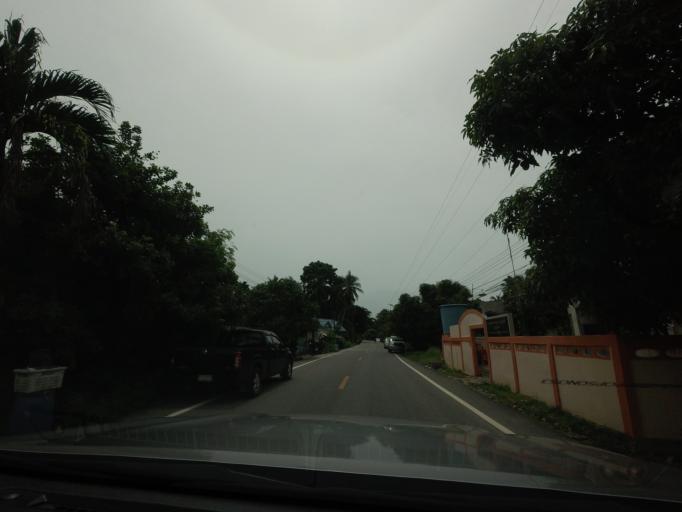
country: TH
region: Pattani
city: Kapho
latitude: 6.6076
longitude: 101.5372
